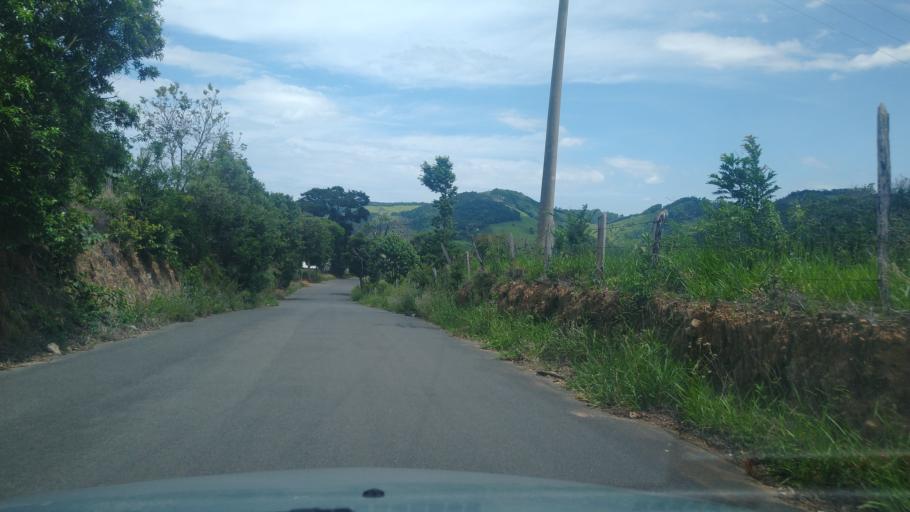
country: BR
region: Minas Gerais
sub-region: Extrema
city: Extrema
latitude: -22.7205
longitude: -46.3320
